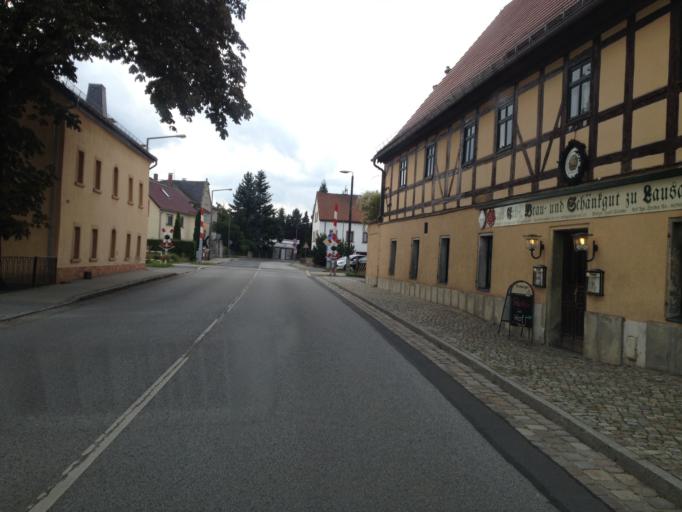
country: DE
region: Saxony
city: Ottendorf-Okrilla
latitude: 51.1512
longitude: 13.8074
